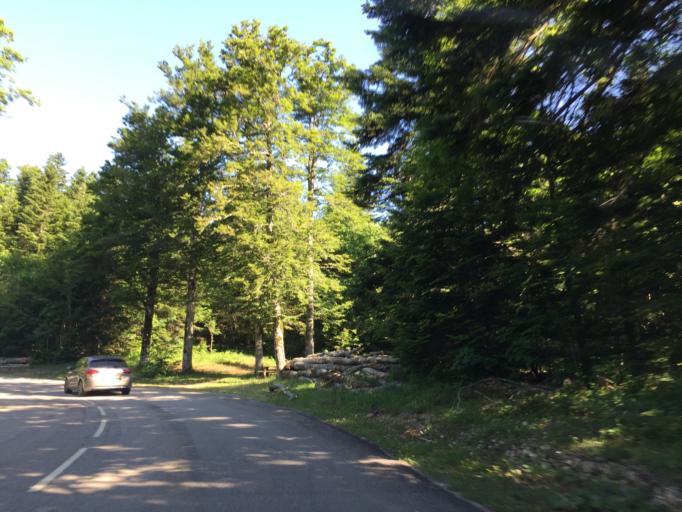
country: FR
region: Rhone-Alpes
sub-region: Departement de la Drome
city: Saint-Jean-en-Royans
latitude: 44.9061
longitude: 5.3406
